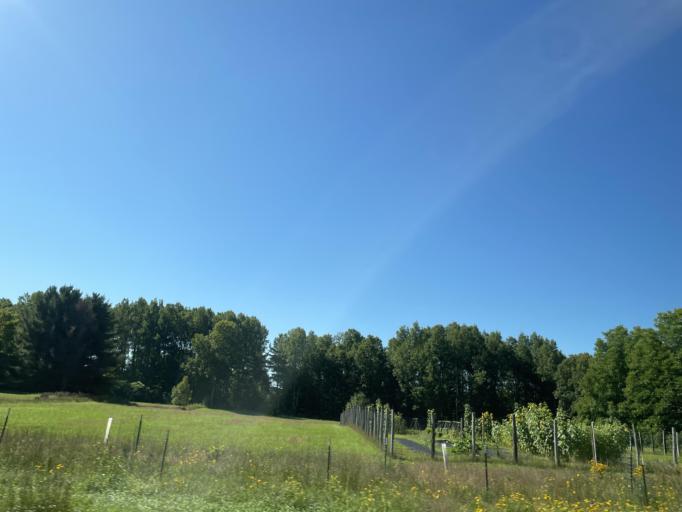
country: US
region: Michigan
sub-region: Benzie County
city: Beulah
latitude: 44.6175
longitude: -86.0845
